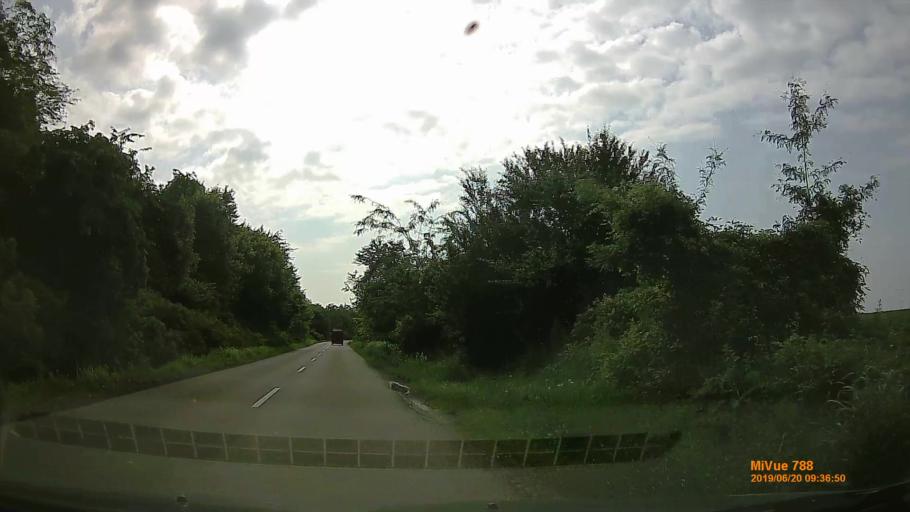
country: HU
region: Baranya
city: Pecsvarad
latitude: 46.1680
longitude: 18.4566
